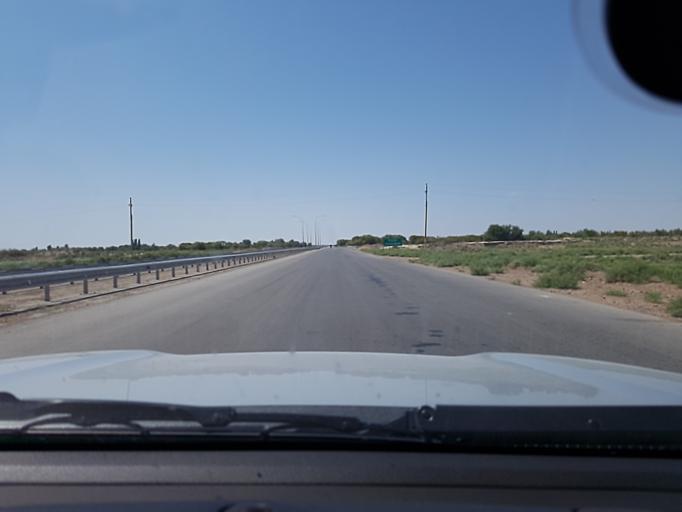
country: TM
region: Dasoguz
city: Yylanly
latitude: 41.7689
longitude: 59.4408
